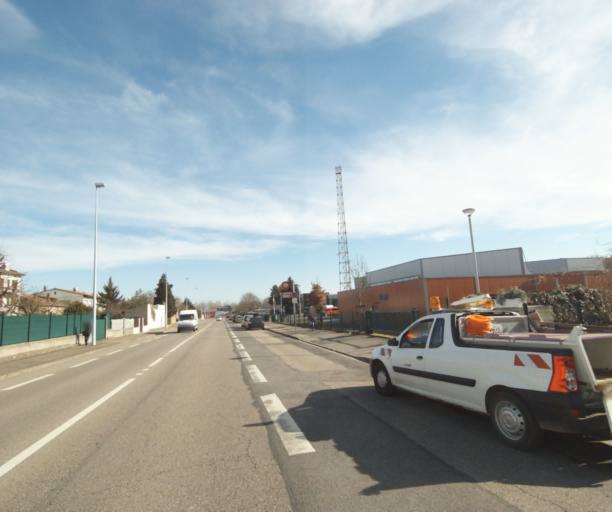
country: FR
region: Lorraine
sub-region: Departement de Meurthe-et-Moselle
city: Vandoeuvre-les-Nancy
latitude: 48.6666
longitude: 6.1840
